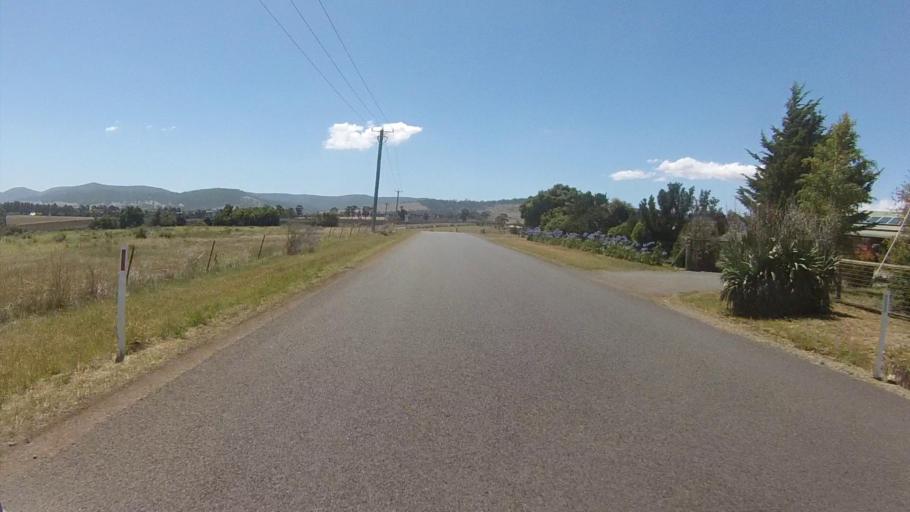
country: AU
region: Tasmania
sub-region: Sorell
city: Sorell
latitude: -42.7774
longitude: 147.5807
